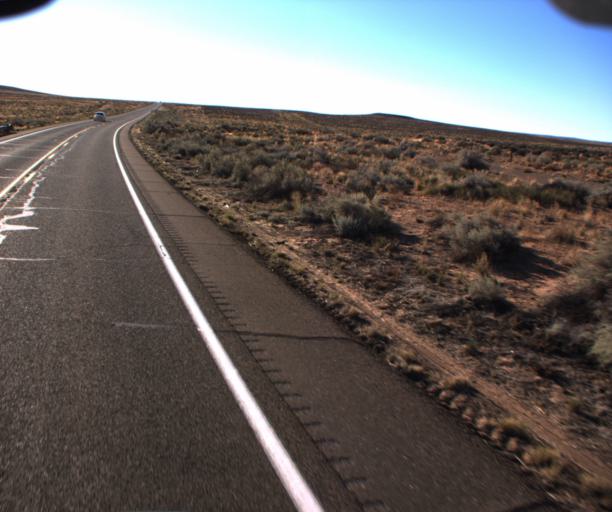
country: US
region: Arizona
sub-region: Coconino County
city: Page
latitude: 36.9763
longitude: -111.5192
